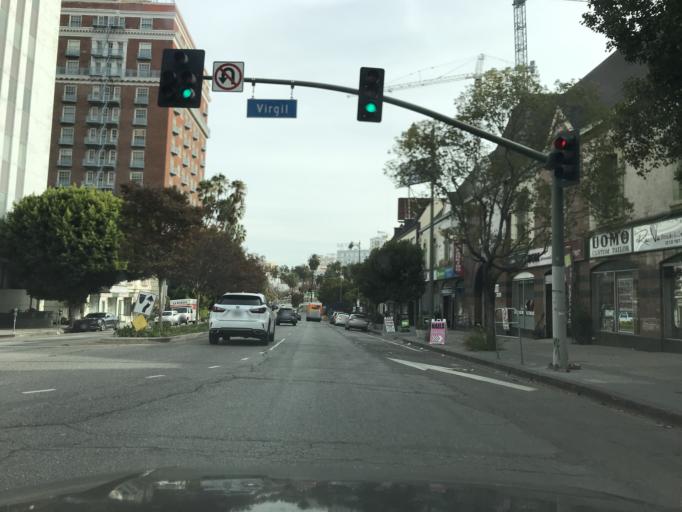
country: US
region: California
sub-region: Los Angeles County
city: Silver Lake
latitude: 34.0617
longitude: -118.2872
